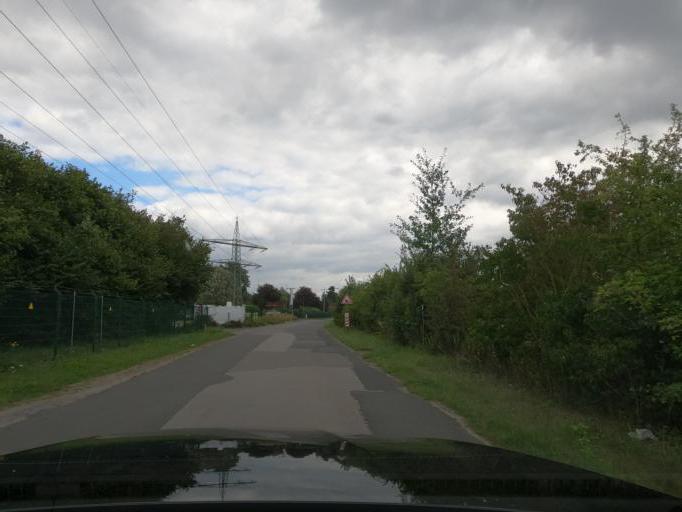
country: DE
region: Lower Saxony
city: Lehrte
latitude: 52.3809
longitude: 9.9534
